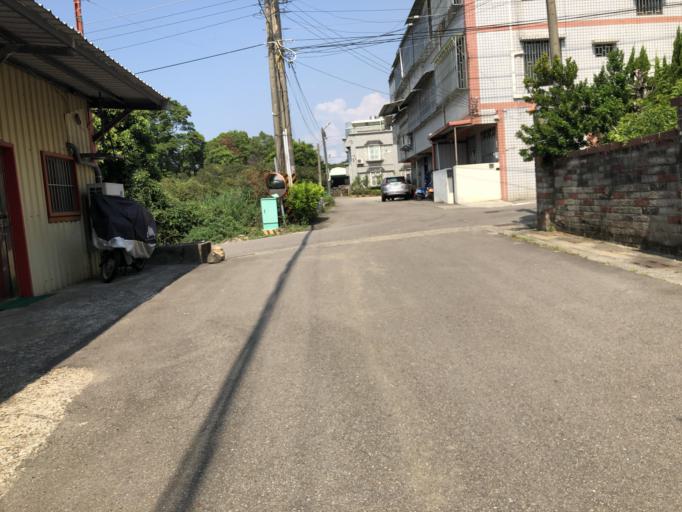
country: TW
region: Taiwan
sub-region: Miaoli
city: Miaoli
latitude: 24.4752
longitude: 120.7954
